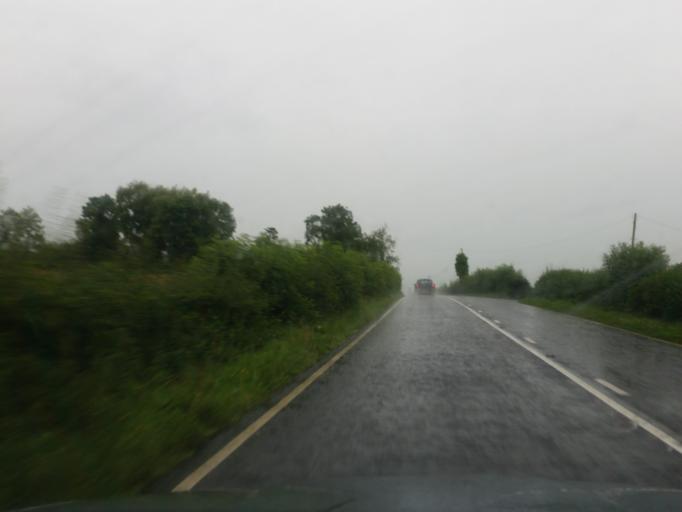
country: GB
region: Northern Ireland
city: Lisnaskea
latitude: 54.2824
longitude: -7.4670
